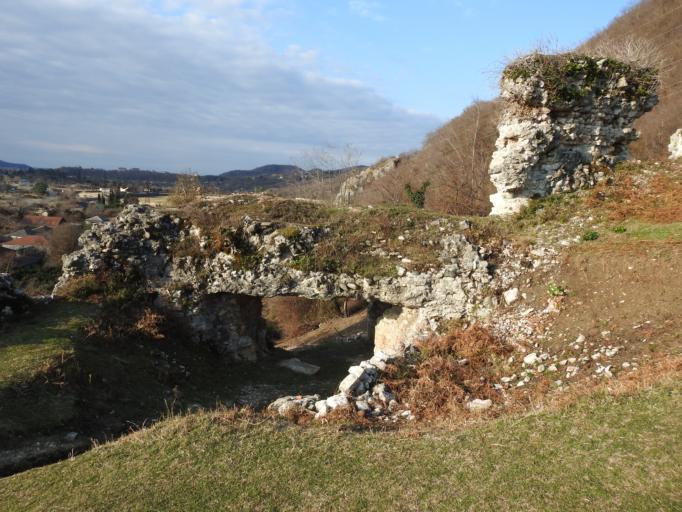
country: GE
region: Abkhazia
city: Bich'vinta
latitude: 43.2405
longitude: 40.3958
